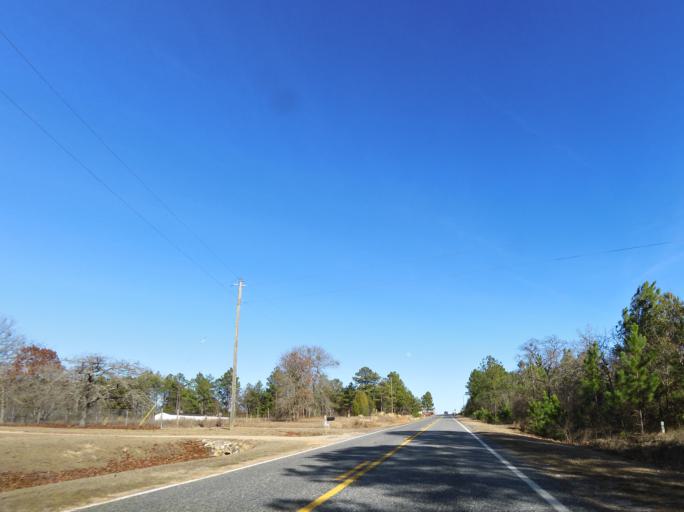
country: US
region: Georgia
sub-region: Crawford County
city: Knoxville
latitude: 32.7281
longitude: -83.9657
